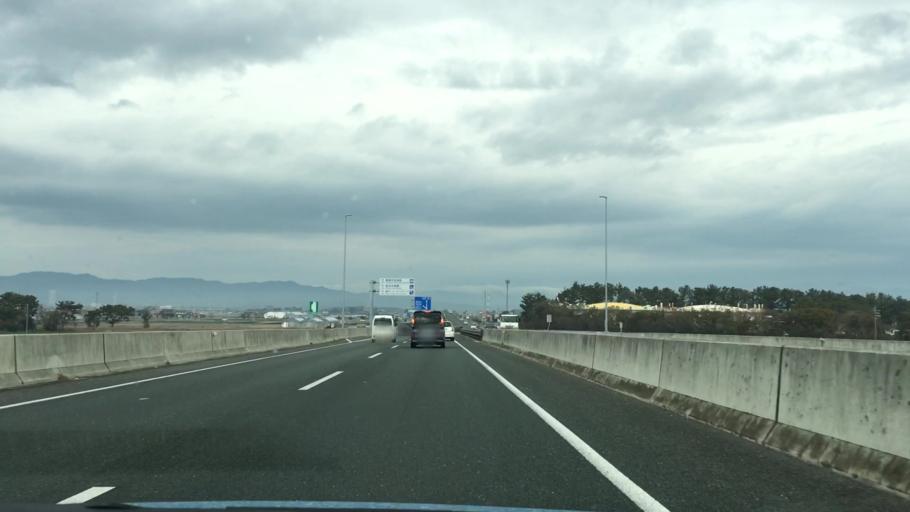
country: JP
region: Aichi
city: Toyohashi
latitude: 34.7548
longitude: 137.3343
